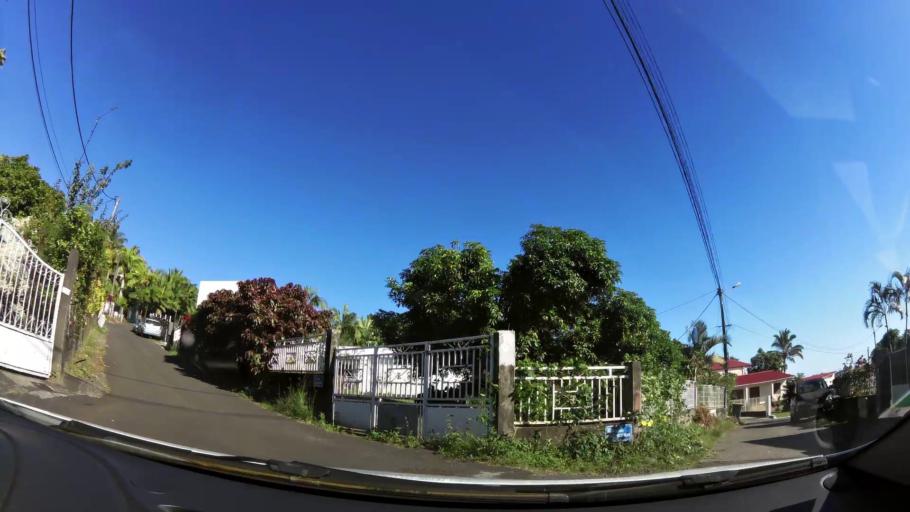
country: RE
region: Reunion
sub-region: Reunion
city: Saint-Denis
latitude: -20.9195
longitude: 55.4731
